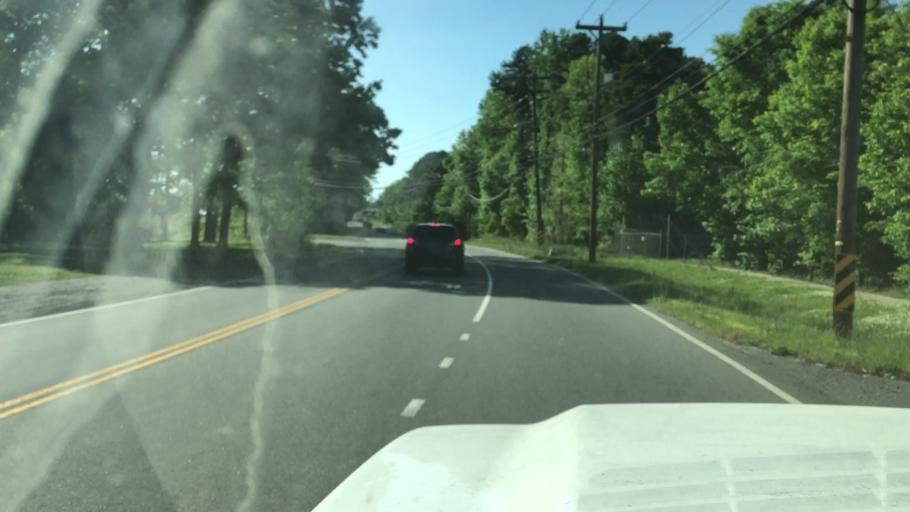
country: US
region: North Carolina
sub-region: Mecklenburg County
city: Charlotte
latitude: 35.2795
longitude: -80.8999
